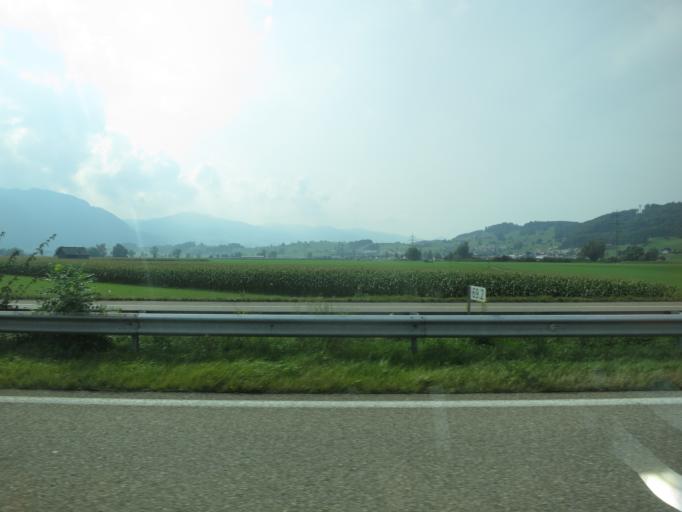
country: CH
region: Schwyz
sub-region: Bezirk March
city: Tuggen
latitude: 47.2058
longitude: 8.9650
